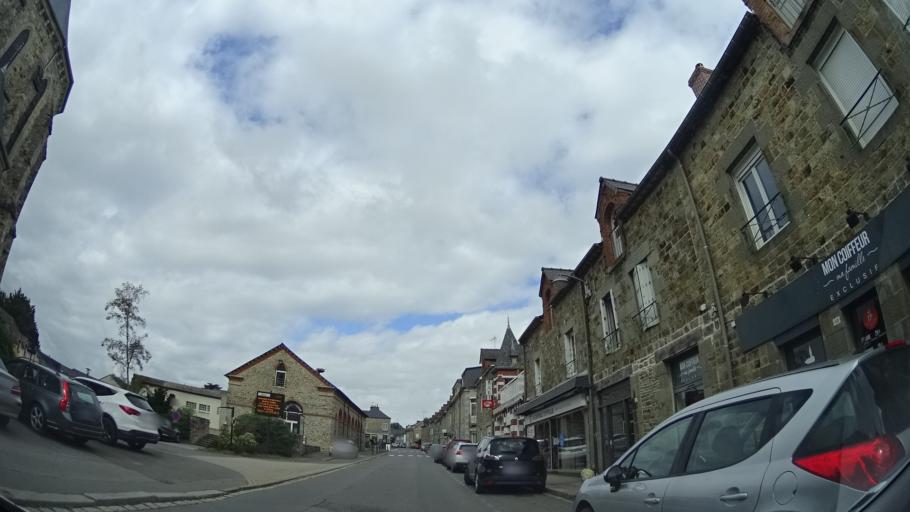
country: FR
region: Brittany
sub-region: Departement d'Ille-et-Vilaine
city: Chasne-sur-Illet
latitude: 48.2624
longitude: -1.6072
